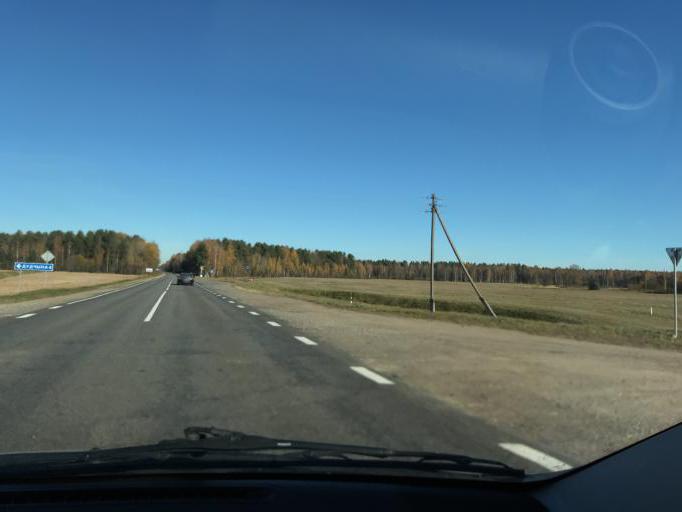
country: BY
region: Vitebsk
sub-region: Ushatski Rayon
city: Ushachy
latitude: 55.0569
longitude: 28.7520
